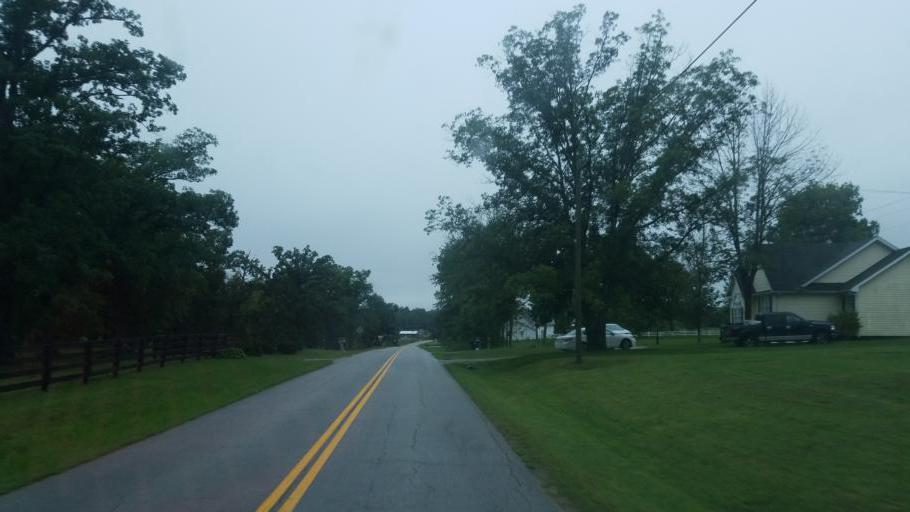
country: US
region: Kentucky
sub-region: Fleming County
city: Flemingsburg
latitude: 38.4048
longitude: -83.6136
